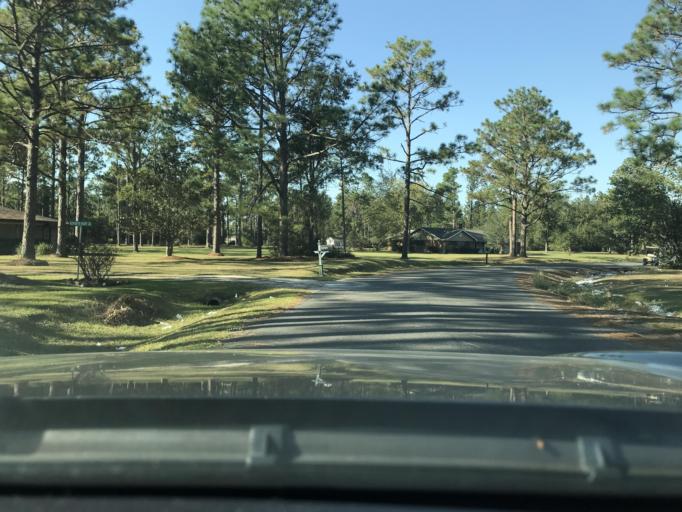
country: US
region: Louisiana
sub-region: Calcasieu Parish
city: Moss Bluff
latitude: 30.3388
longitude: -93.2615
